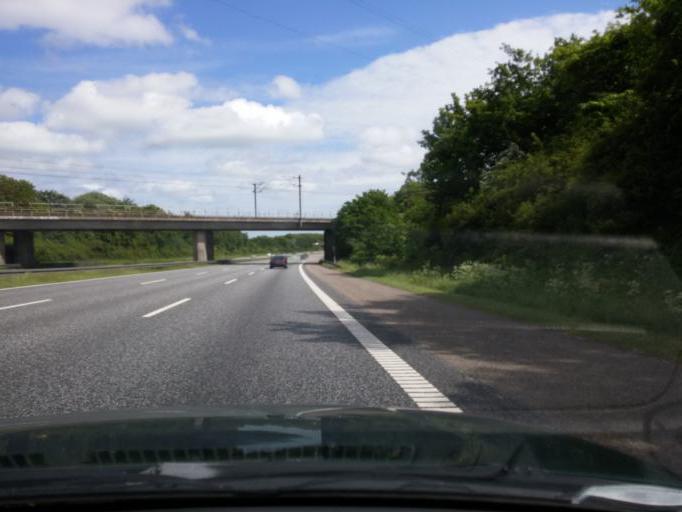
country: DK
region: South Denmark
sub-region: Fredericia Kommune
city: Snoghoj
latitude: 55.5353
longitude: 9.7078
